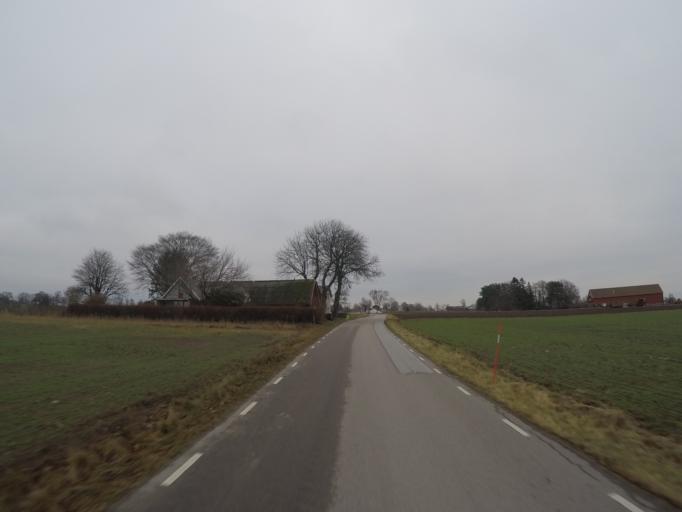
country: SE
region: Skane
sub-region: Hoors Kommun
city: Loberod
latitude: 55.7478
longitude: 13.4476
